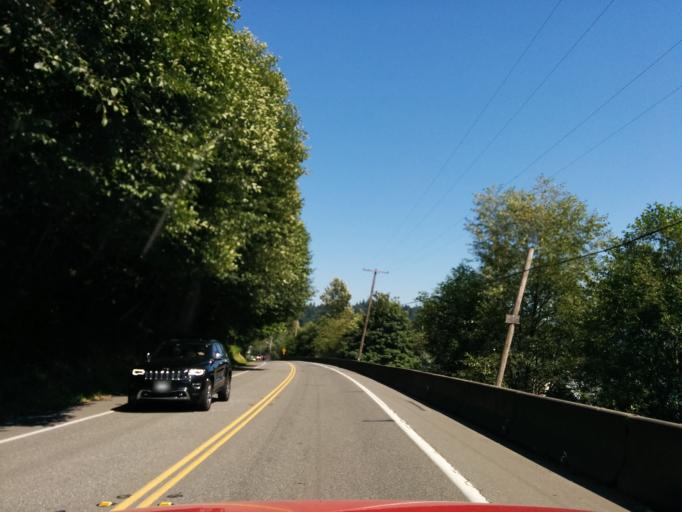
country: US
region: Washington
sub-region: King County
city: West Lake Sammamish
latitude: 47.5692
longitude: -122.0617
